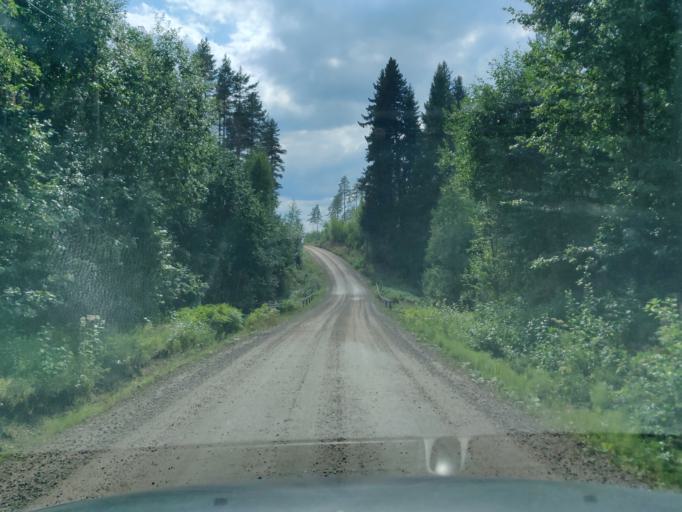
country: SE
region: Vaermland
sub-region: Hagfors Kommun
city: Hagfors
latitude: 59.9868
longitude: 13.5611
